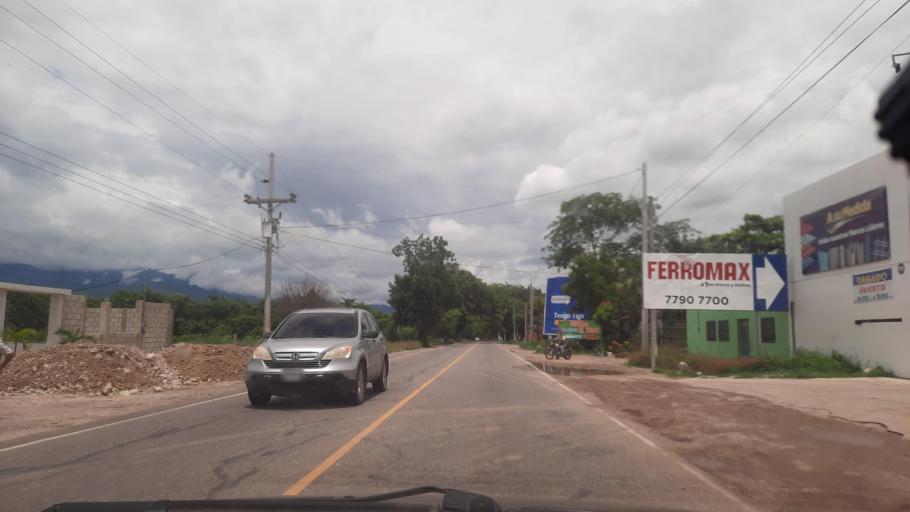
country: GT
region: Zacapa
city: Estanzuela
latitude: 14.9897
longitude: -89.5633
